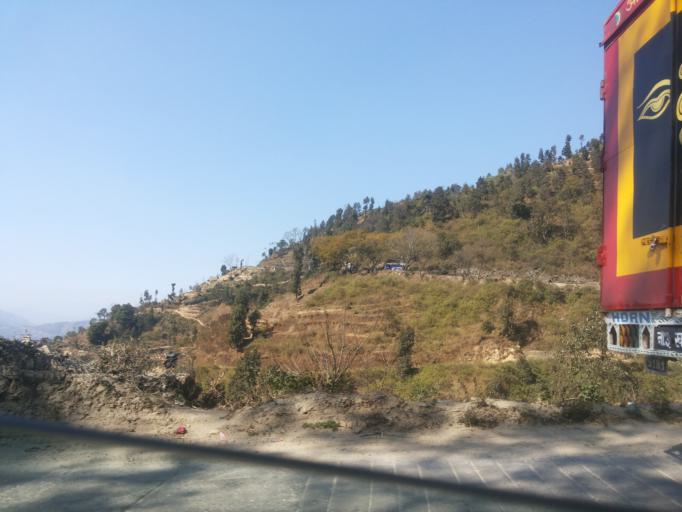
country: NP
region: Central Region
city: Kirtipur
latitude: 27.7103
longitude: 85.2016
